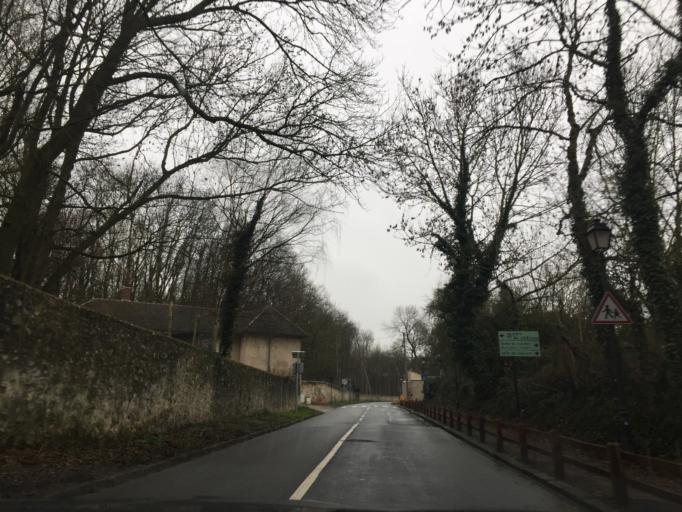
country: FR
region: Ile-de-France
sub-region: Departement de Seine-et-Marne
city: Coupvray
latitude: 48.8877
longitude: 2.7924
